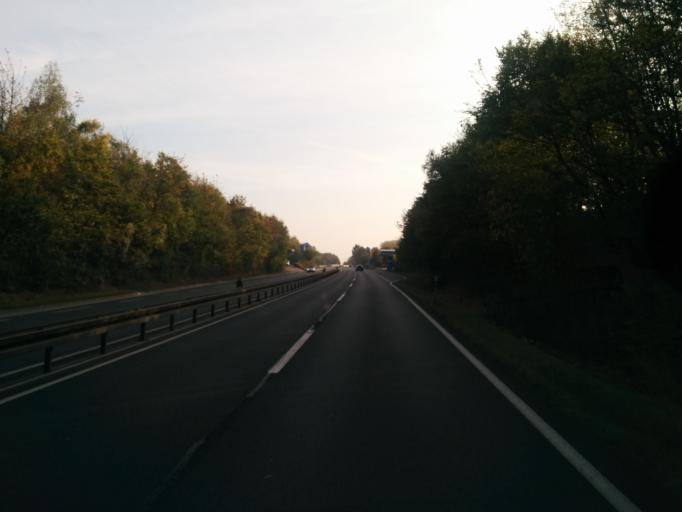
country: DE
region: Lower Saxony
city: Laatzen
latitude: 52.3572
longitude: 9.8592
